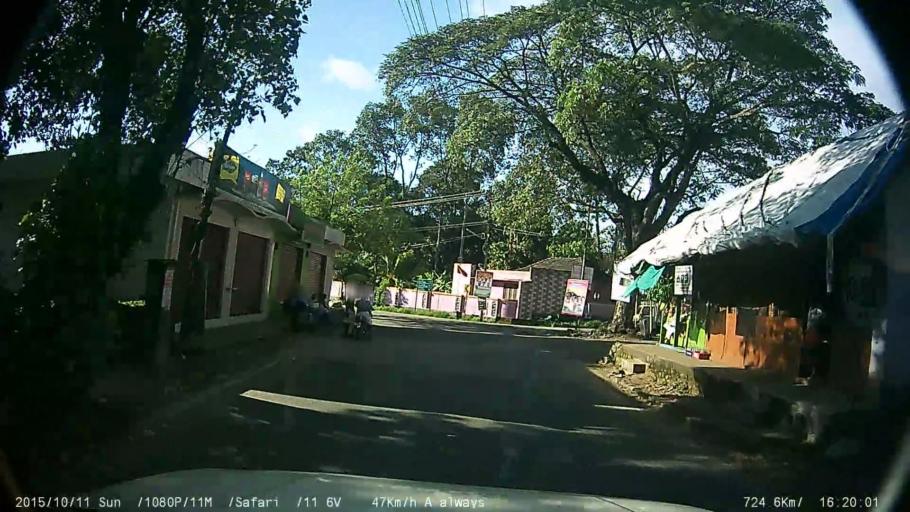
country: IN
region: Kerala
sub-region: Kottayam
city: Palackattumala
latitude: 9.7480
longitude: 76.6095
